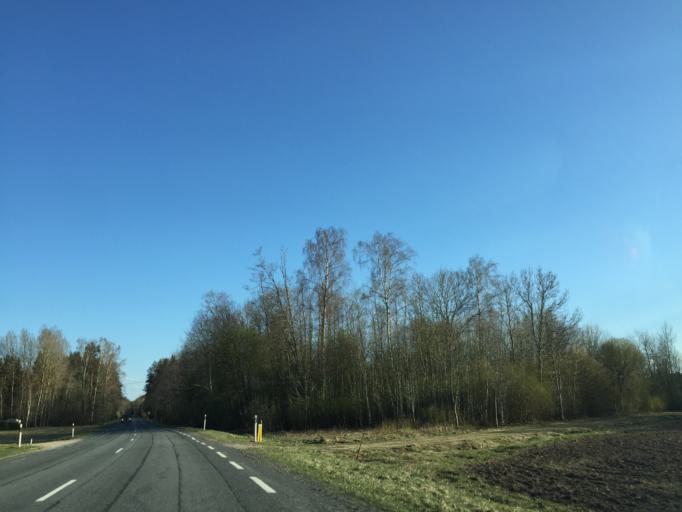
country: EE
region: Valgamaa
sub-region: Torva linn
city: Torva
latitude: 58.1814
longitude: 25.9545
